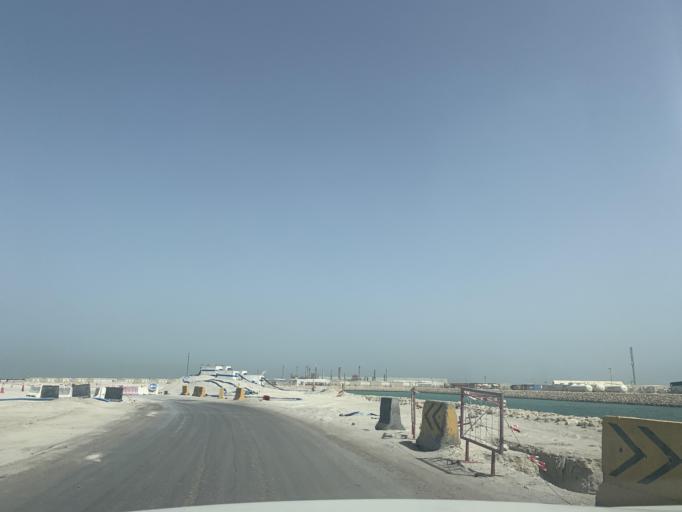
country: BH
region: Northern
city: Sitrah
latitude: 26.1556
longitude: 50.6331
